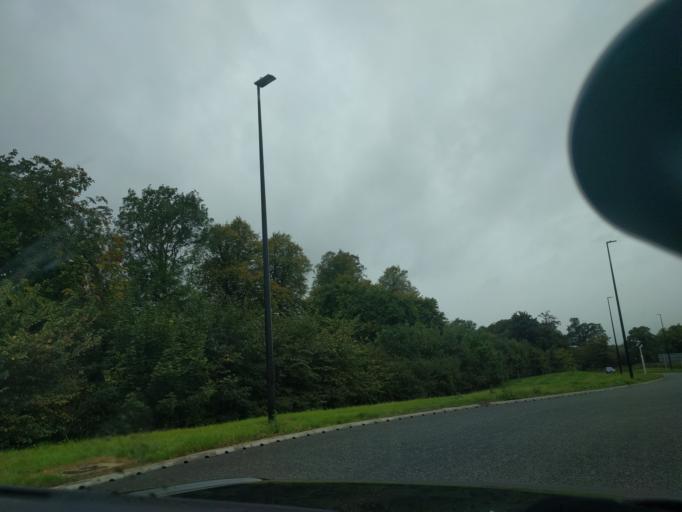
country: GB
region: England
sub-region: North Yorkshire
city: Bedale
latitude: 54.2925
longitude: -1.5972
